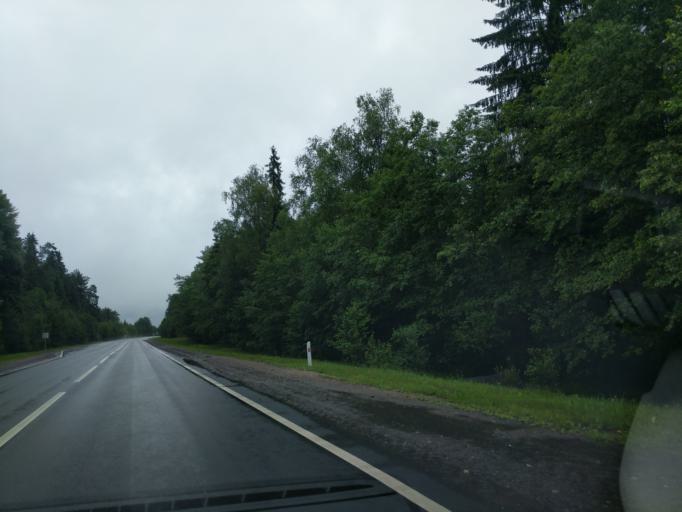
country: BY
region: Minsk
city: Syomkava
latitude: 54.1719
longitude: 27.4994
